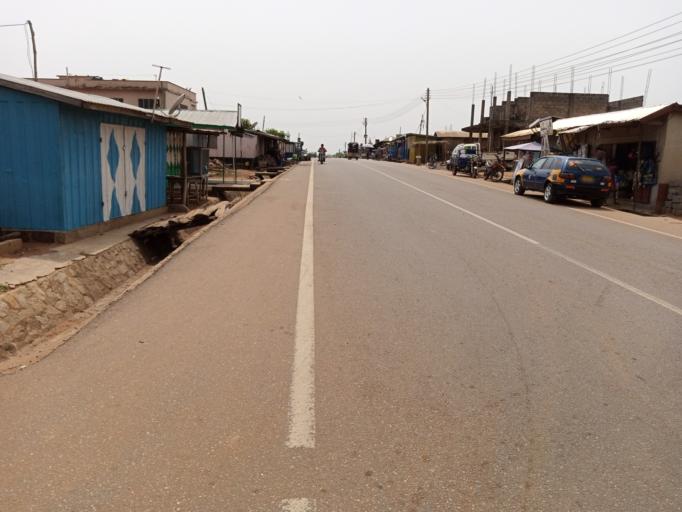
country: GH
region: Volta
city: Kpandu
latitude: 7.0033
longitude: 0.2954
